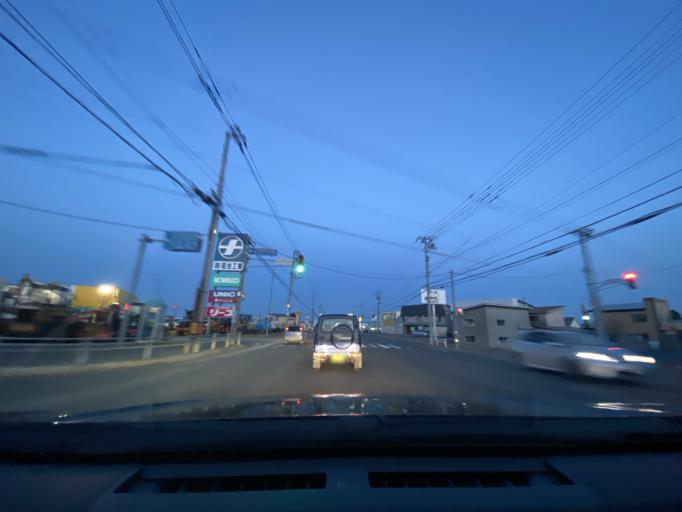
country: JP
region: Hokkaido
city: Kitami
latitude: 43.7994
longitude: 143.8289
